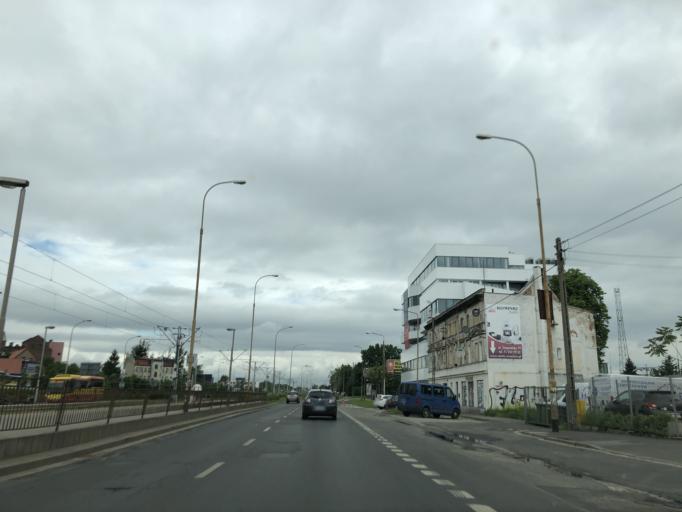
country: PL
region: Lower Silesian Voivodeship
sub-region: Powiat wroclawski
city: Wroclaw
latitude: 51.1406
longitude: 17.0325
